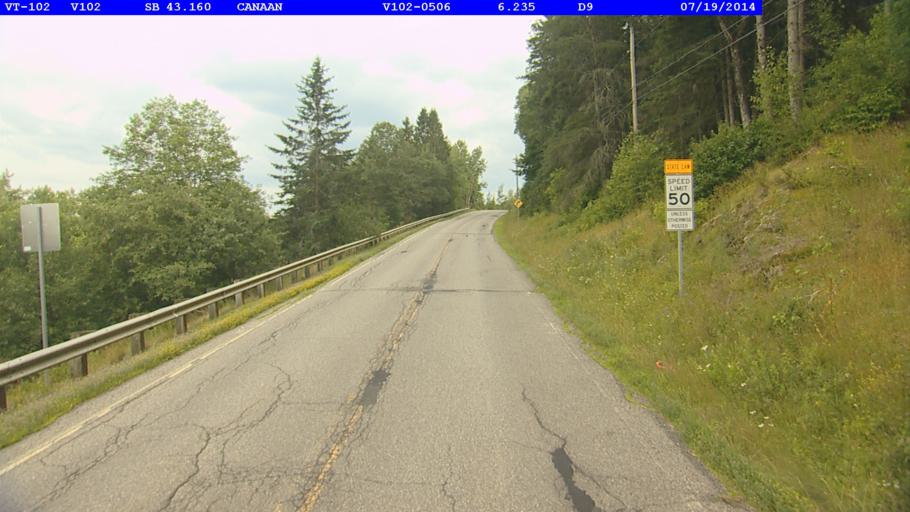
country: US
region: New Hampshire
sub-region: Coos County
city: Colebrook
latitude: 44.9885
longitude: -71.5421
